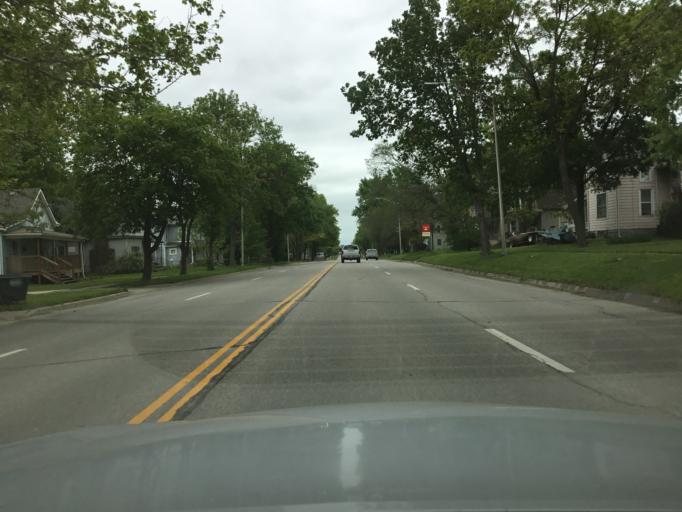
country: US
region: Kansas
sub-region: Franklin County
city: Ottawa
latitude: 38.6057
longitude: -95.2687
